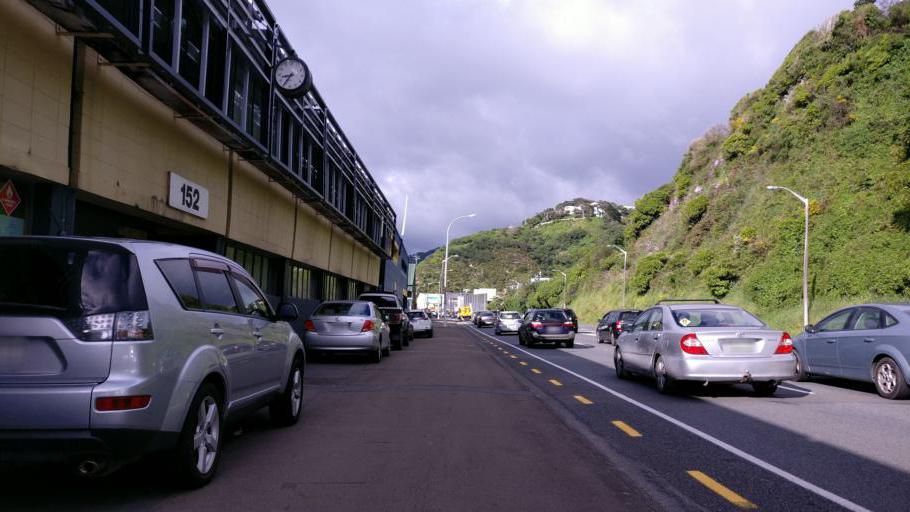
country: NZ
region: Wellington
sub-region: Wellington City
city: Wellington
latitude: -41.2578
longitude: 174.7931
